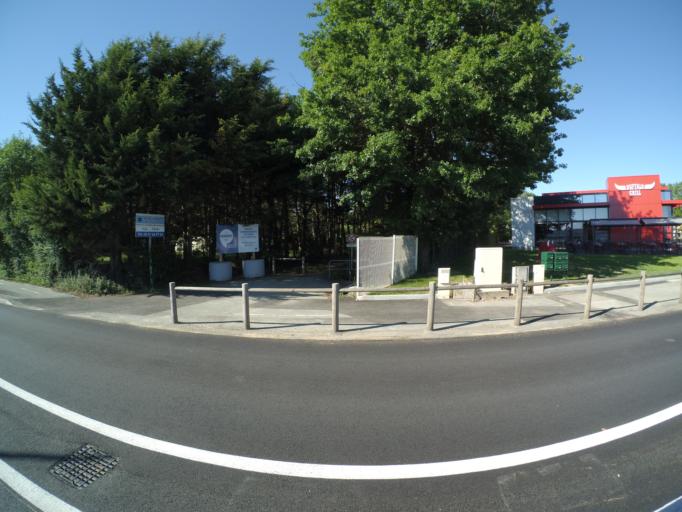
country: FR
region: Pays de la Loire
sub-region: Departement de la Vendee
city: Les Herbiers
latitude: 46.8755
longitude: -1.0257
